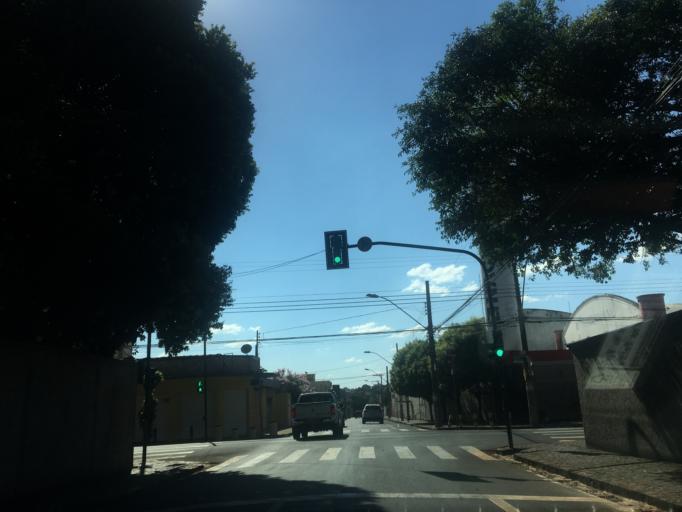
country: BR
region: Minas Gerais
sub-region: Uberlandia
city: Uberlandia
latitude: -18.9077
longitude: -48.2772
